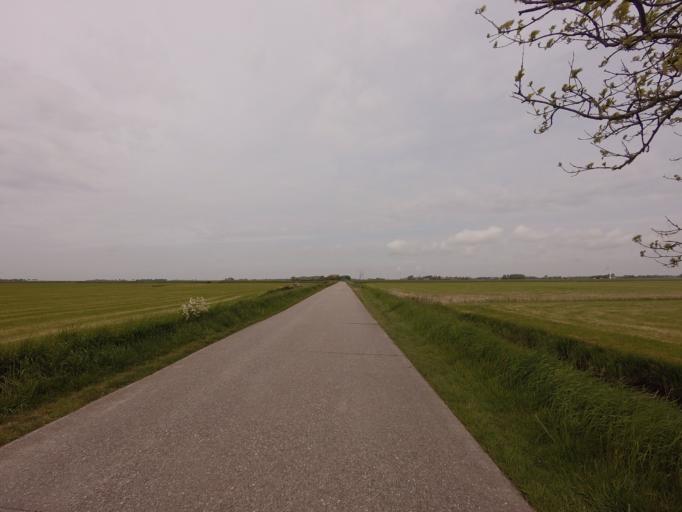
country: NL
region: Friesland
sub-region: Sudwest Fryslan
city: Makkum
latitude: 53.0660
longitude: 5.4592
